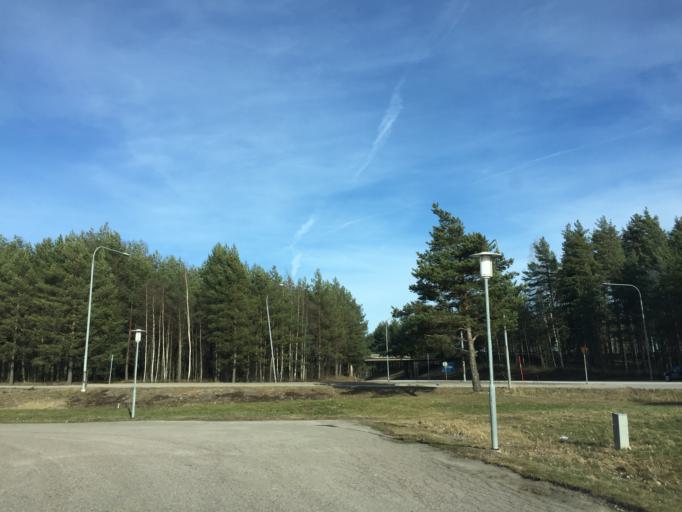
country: SE
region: OErebro
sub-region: Kumla Kommun
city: Kumla
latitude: 59.2147
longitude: 15.1423
